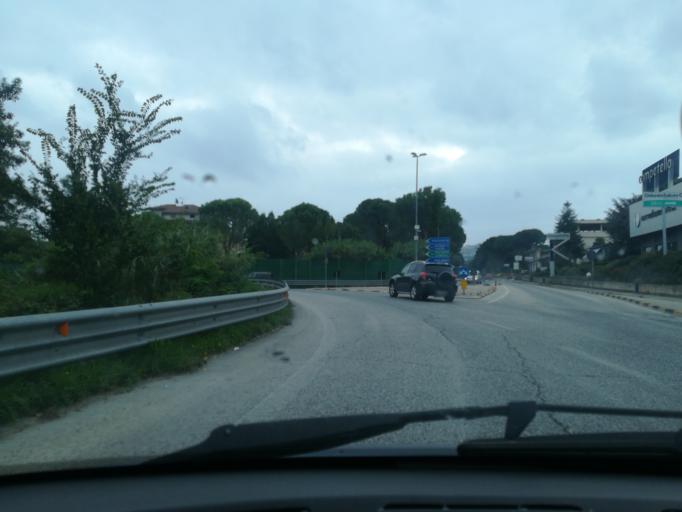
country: IT
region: The Marches
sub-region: Provincia di Macerata
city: Zona Industriale
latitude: 43.2656
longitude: 13.4891
